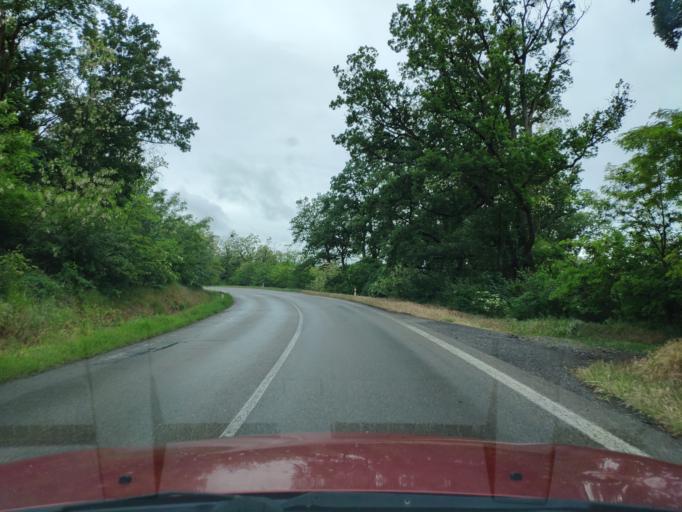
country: HU
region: Borsod-Abauj-Zemplen
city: Ricse
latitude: 48.4413
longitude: 21.9400
